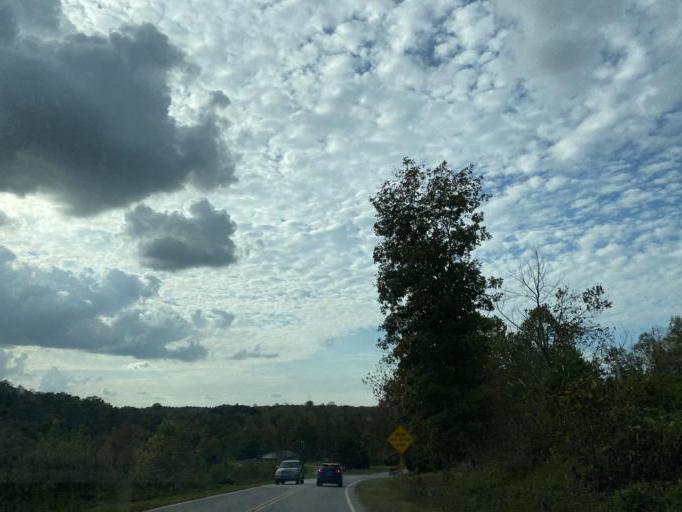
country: US
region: South Carolina
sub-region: Cherokee County
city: Gaffney
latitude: 35.0714
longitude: -81.7209
